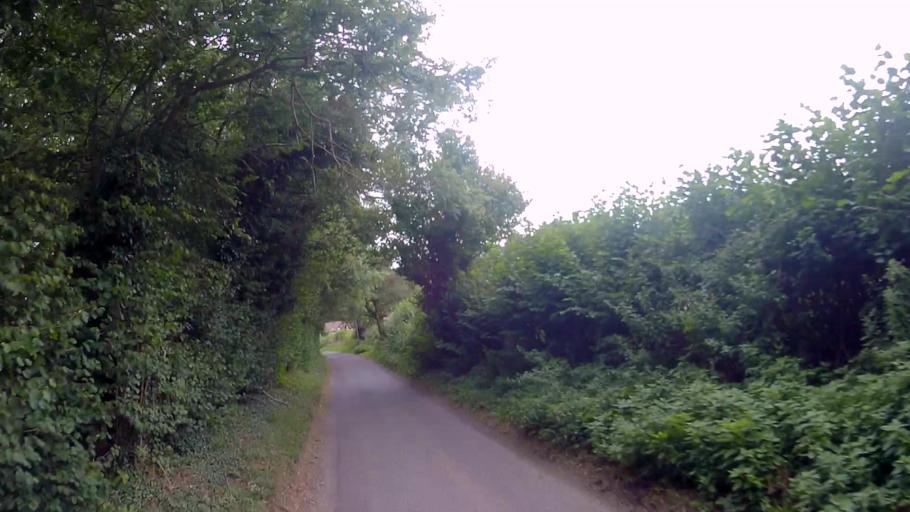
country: GB
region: England
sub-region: Hampshire
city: Overton
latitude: 51.2134
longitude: -1.2290
